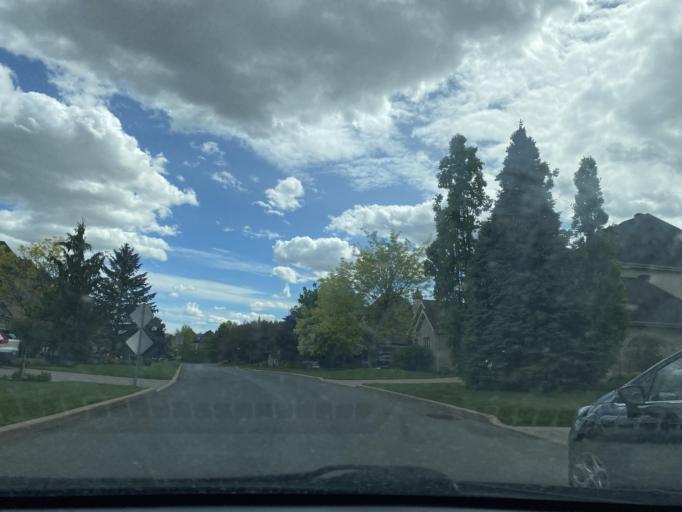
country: CA
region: Quebec
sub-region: Monteregie
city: Carignan
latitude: 45.4707
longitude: -73.2956
